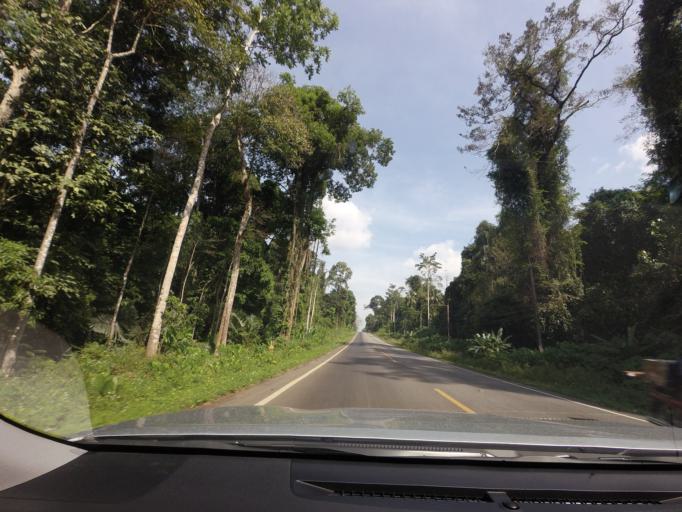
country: TH
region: Krabi
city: Krabi
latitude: 8.1426
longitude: 98.8396
